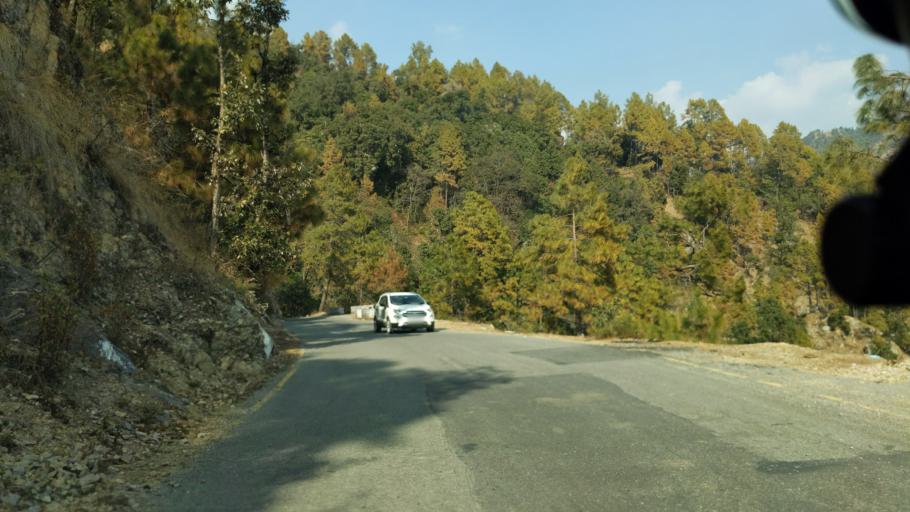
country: IN
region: Uttarakhand
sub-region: Naini Tal
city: Bhowali
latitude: 29.4012
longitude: 79.5348
